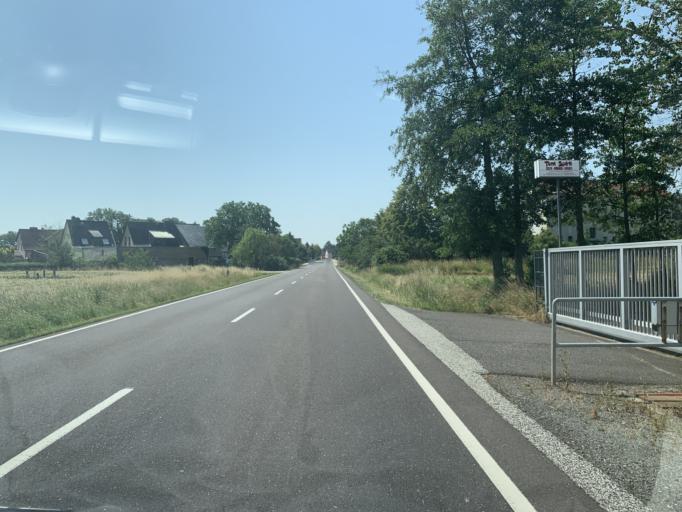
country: DE
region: Saxony-Anhalt
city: Erxleben
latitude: 52.2256
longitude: 11.2418
